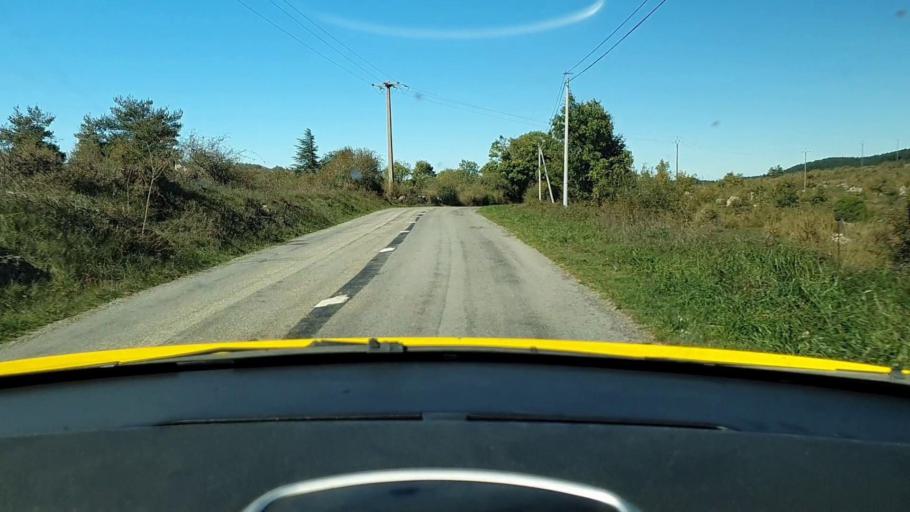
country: FR
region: Languedoc-Roussillon
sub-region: Departement du Gard
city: Aveze
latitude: 43.9577
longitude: 3.4110
